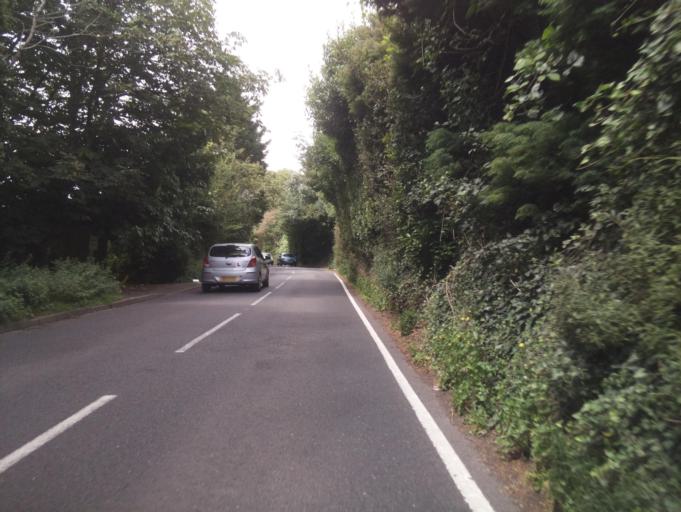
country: GB
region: England
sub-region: Devon
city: Teignmouth
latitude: 50.5637
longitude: -3.5052
